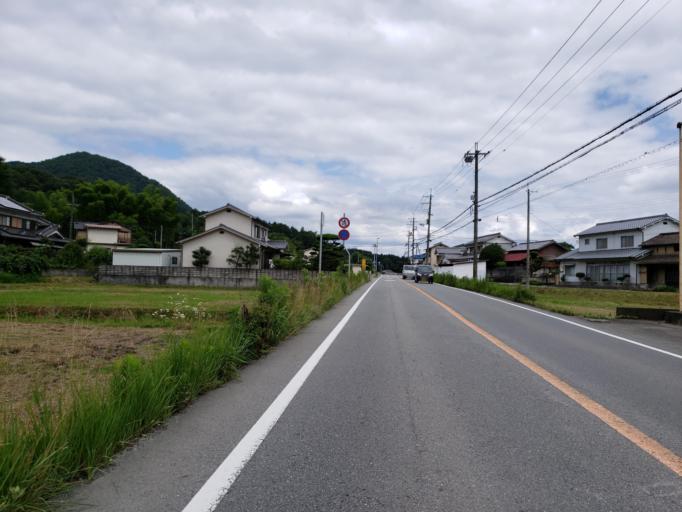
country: JP
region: Hyogo
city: Himeji
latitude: 34.9608
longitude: 134.7036
